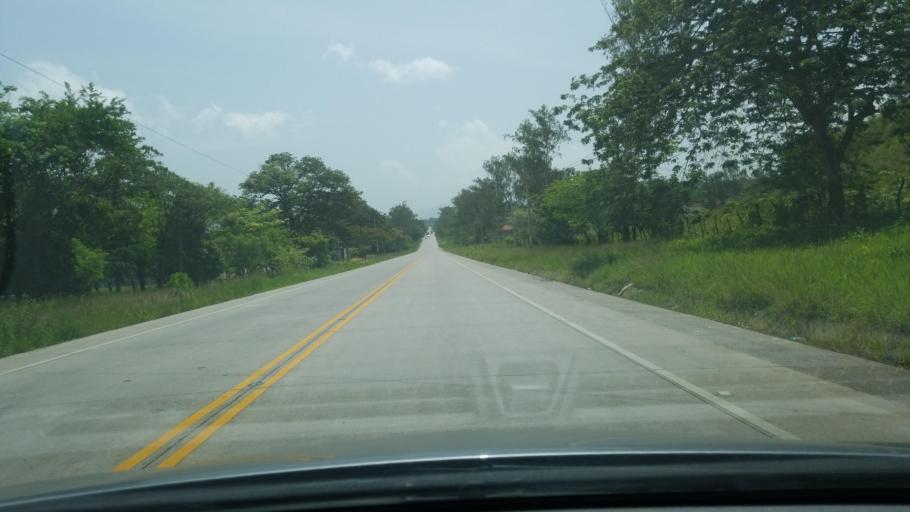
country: HN
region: Copan
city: Florida
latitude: 15.0404
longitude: -88.8179
